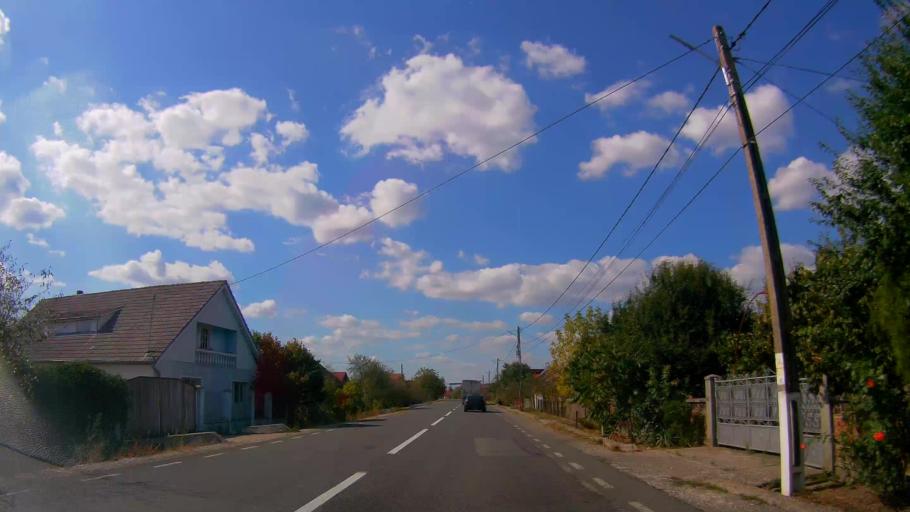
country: RO
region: Salaj
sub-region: Comuna Bocsa
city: Bocsa
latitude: 47.3166
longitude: 22.9076
